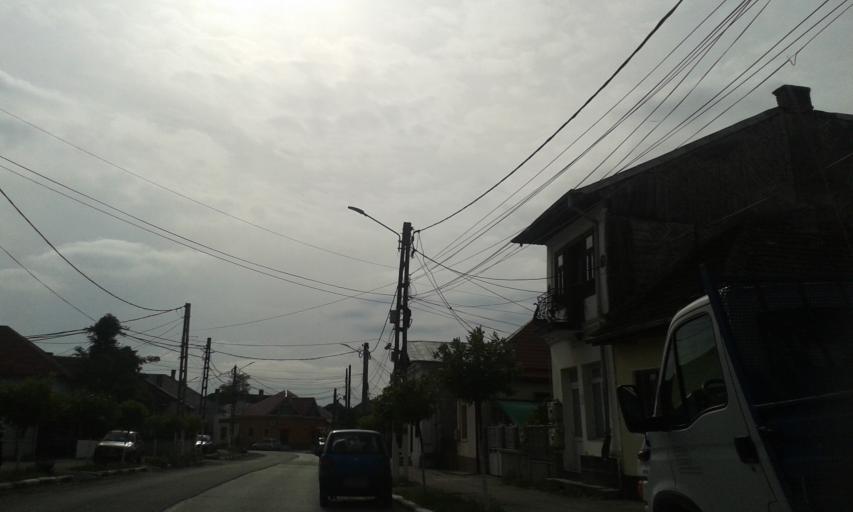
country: RO
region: Gorj
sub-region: Comuna Targu Carbunesti
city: Targu Carbunesti
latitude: 44.9532
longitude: 23.5138
